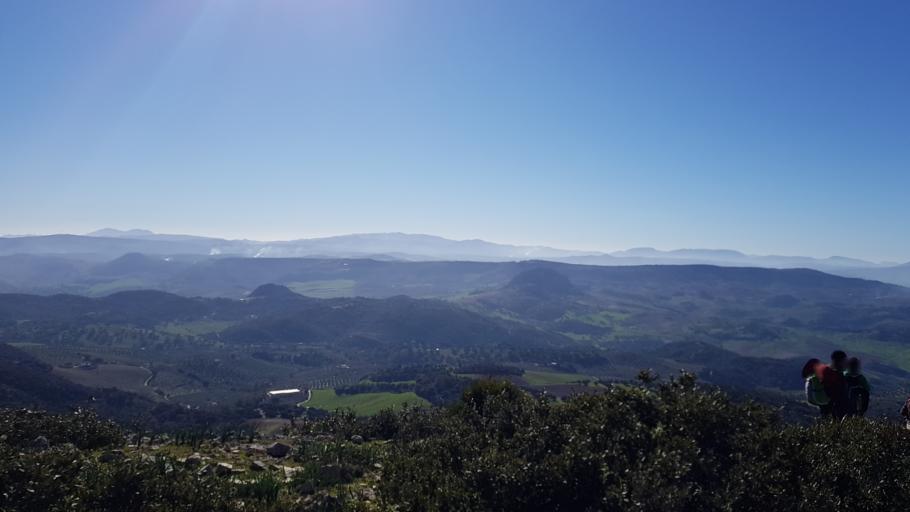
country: ES
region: Andalusia
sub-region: Provincia de Sevilla
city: Pruna
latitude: 36.9965
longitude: -5.1961
